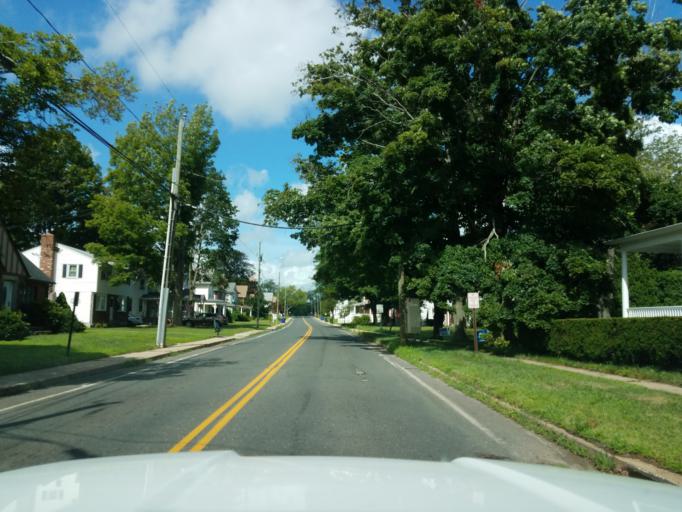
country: US
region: Connecticut
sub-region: Hartford County
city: Windsor Locks
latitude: 41.9308
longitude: -72.6331
